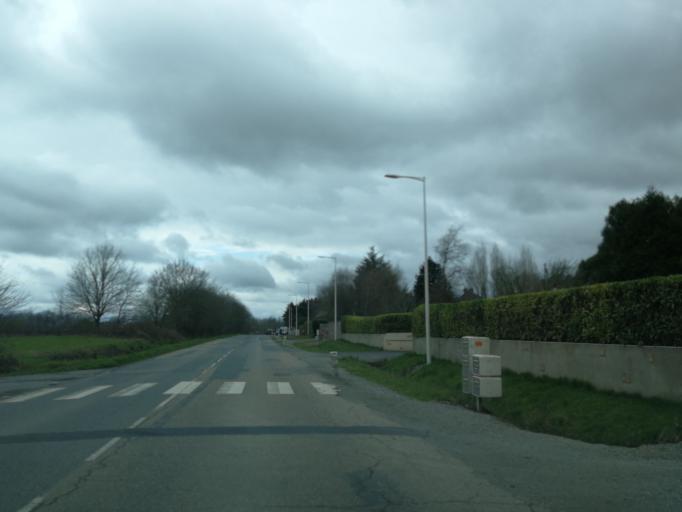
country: FR
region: Brittany
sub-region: Departement d'Ille-et-Vilaine
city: Guichen
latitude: 47.9608
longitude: -1.8072
